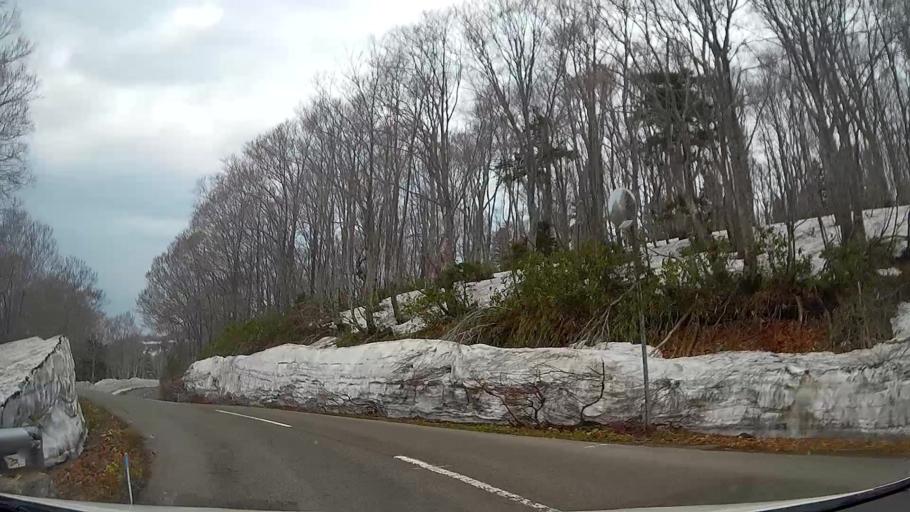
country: JP
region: Aomori
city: Aomori Shi
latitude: 40.6451
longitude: 140.8589
